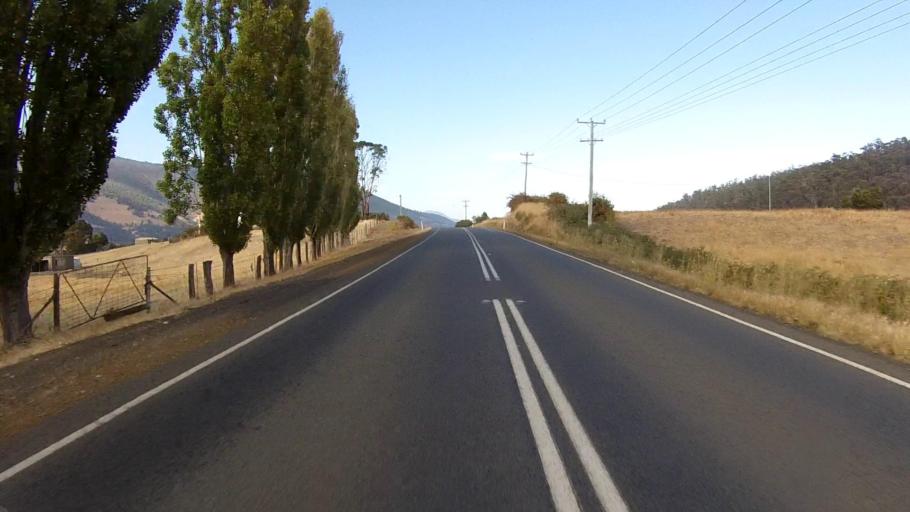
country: AU
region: Tasmania
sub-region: Brighton
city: Bridgewater
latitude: -42.7353
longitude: 147.1746
